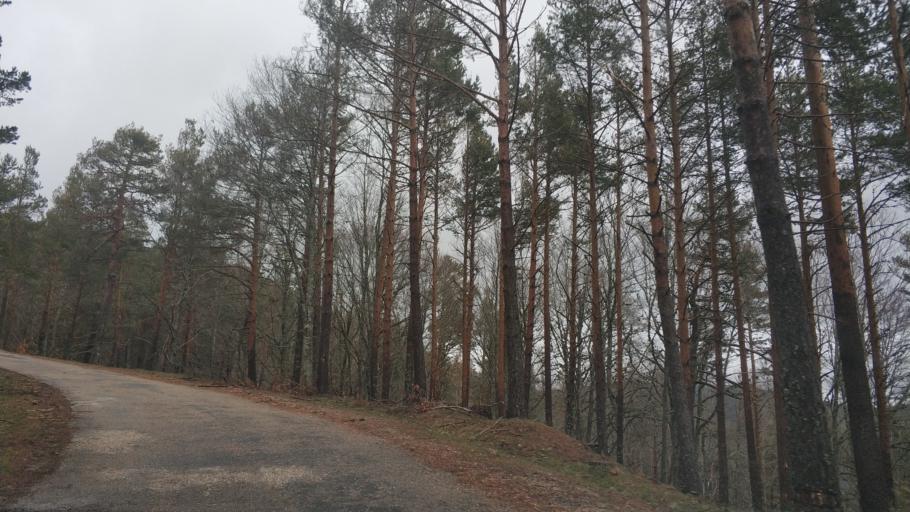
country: ES
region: Castille and Leon
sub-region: Provincia de Burgos
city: Neila
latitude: 42.0444
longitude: -3.0162
